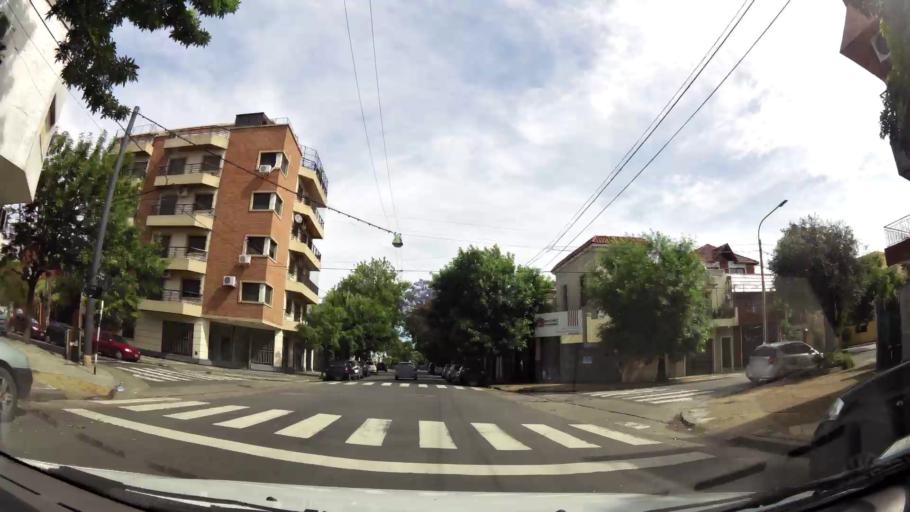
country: AR
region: Buenos Aires
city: San Justo
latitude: -34.6455
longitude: -58.5204
